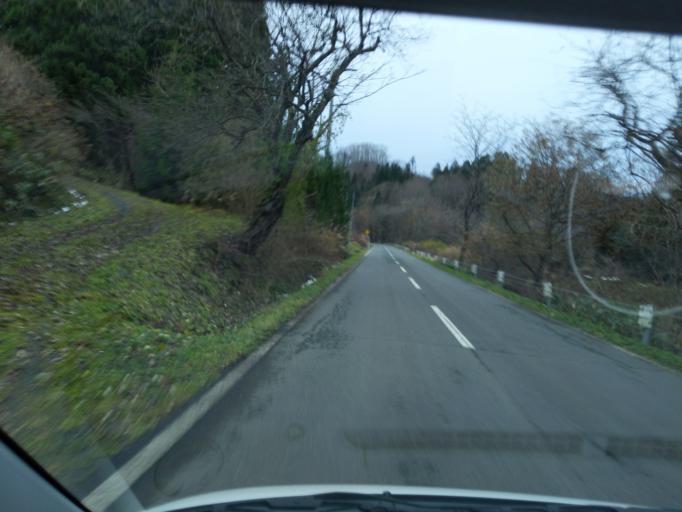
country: JP
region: Iwate
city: Tono
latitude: 39.1605
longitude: 141.3650
